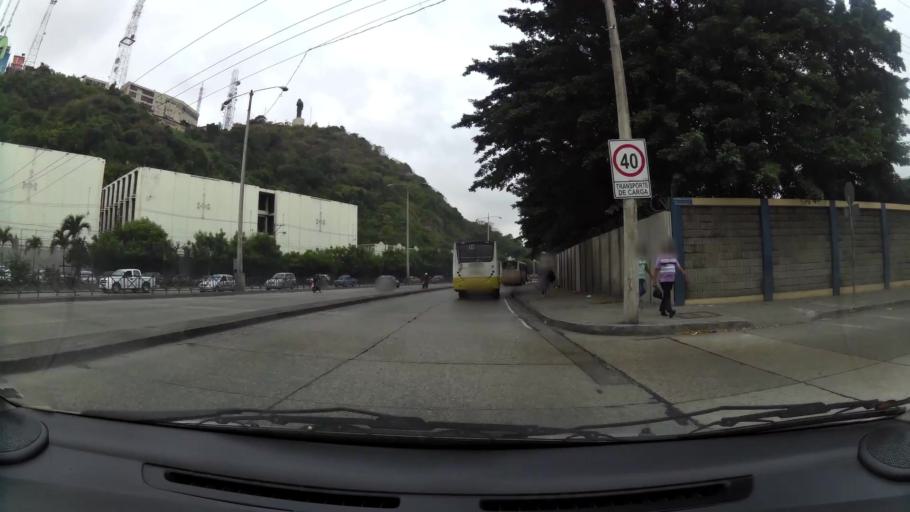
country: EC
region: Guayas
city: Eloy Alfaro
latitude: -2.1782
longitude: -79.8824
